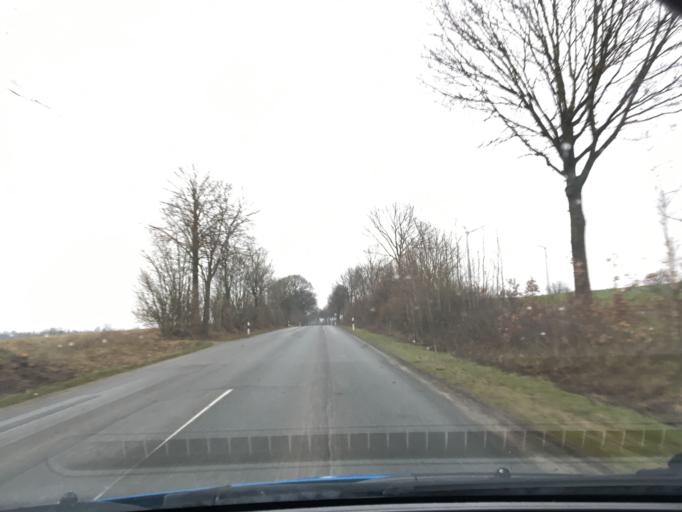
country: DE
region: Schleswig-Holstein
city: Woltersdorf
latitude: 53.5837
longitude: 10.6405
